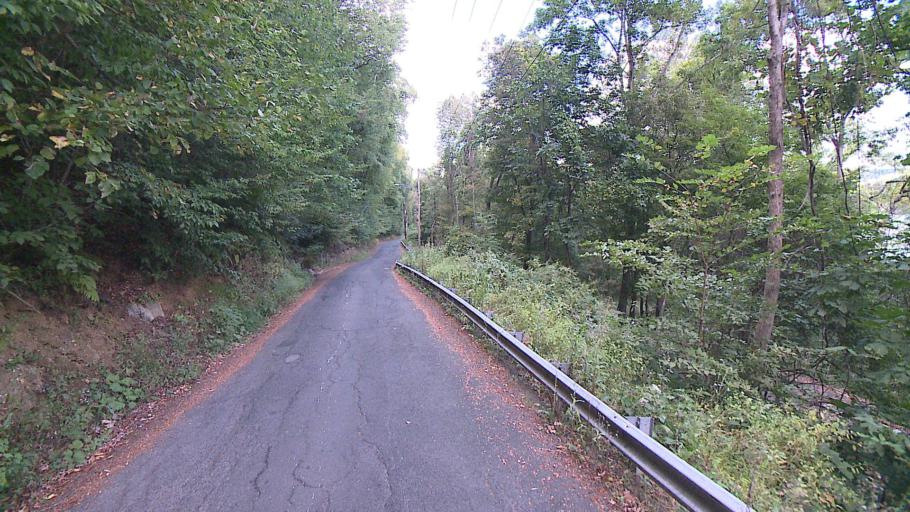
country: US
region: Connecticut
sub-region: Fairfield County
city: Shelton
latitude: 41.3524
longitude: -73.1393
